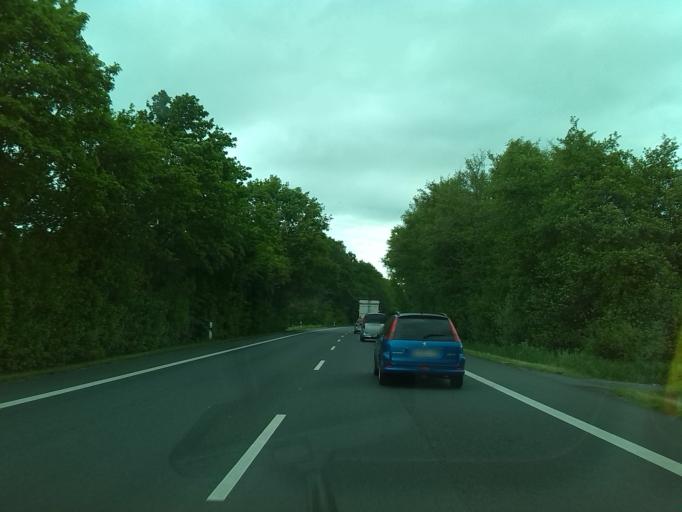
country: DE
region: Hesse
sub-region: Regierungsbezirk Darmstadt
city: Erzhausen
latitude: 49.9375
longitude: 8.6622
